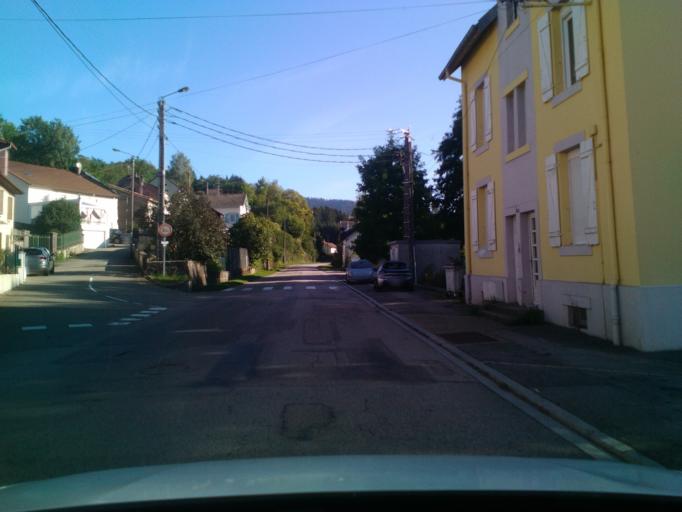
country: FR
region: Lorraine
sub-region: Departement des Vosges
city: Senones
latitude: 48.4078
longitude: 6.9955
